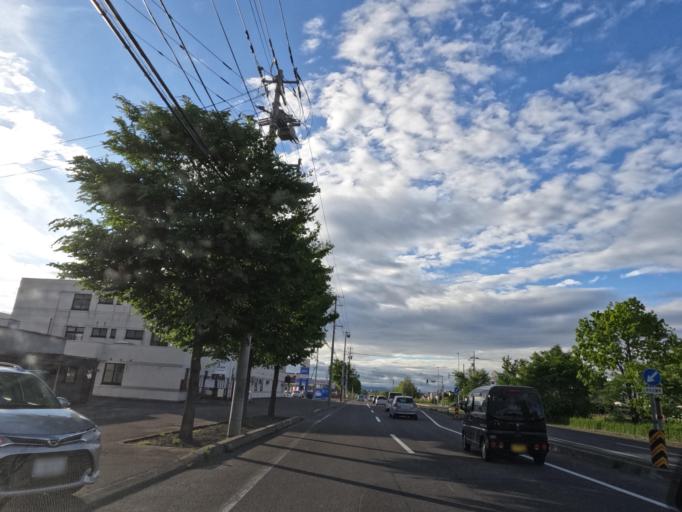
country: JP
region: Hokkaido
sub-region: Asahikawa-shi
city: Asahikawa
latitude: 43.7343
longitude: 142.3633
